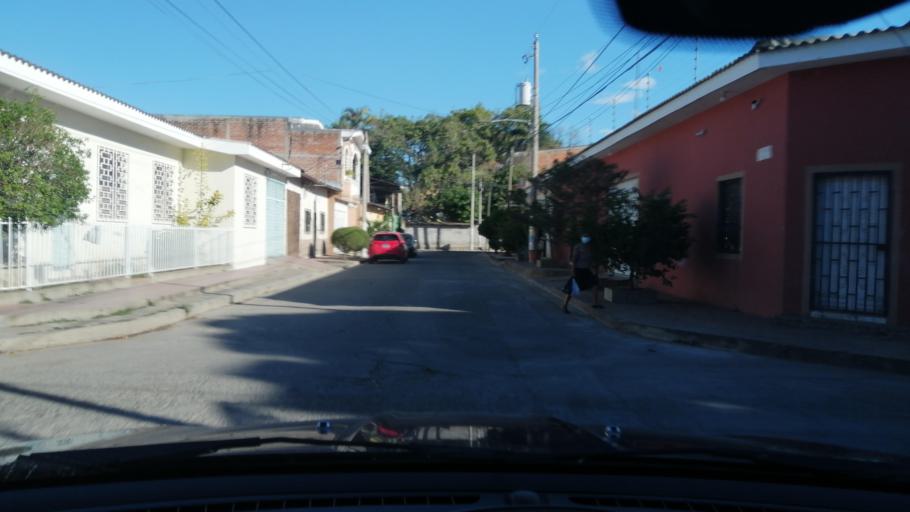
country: SV
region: Santa Ana
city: Metapan
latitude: 14.3352
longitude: -89.4487
